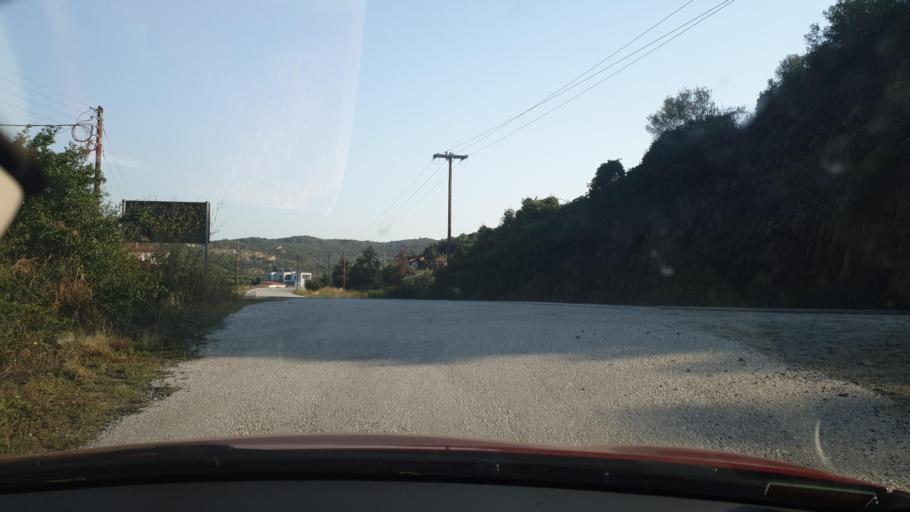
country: GR
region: Central Macedonia
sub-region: Nomos Chalkidikis
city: Sykia
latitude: 39.9826
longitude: 23.9096
